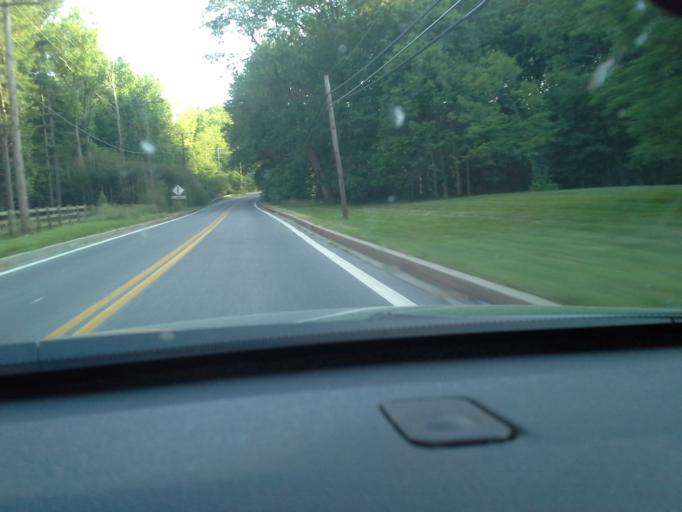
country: US
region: Maryland
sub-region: Anne Arundel County
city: Shady Side
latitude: 38.8403
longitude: -76.5612
